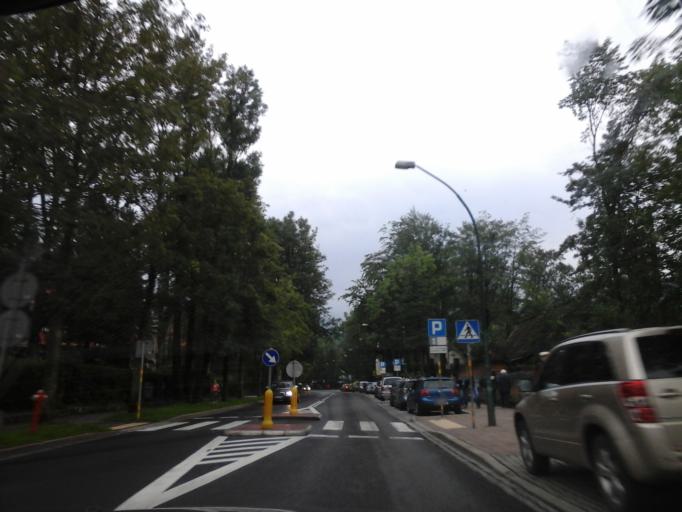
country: PL
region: Lesser Poland Voivodeship
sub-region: Powiat tatrzanski
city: Zakopane
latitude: 49.2894
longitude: 19.9641
